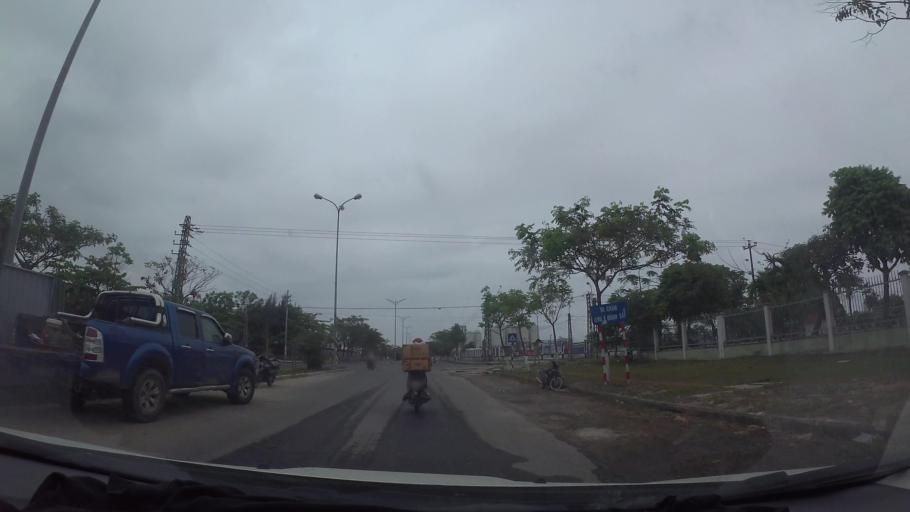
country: VN
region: Da Nang
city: Lien Chieu
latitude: 16.0768
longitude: 108.1396
